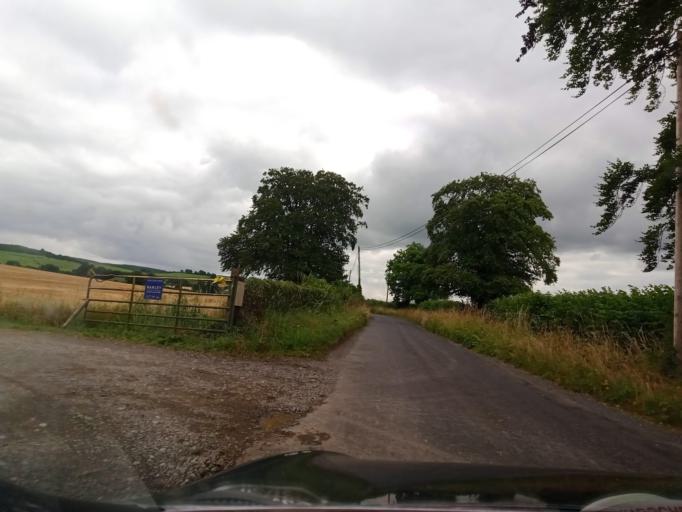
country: IE
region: Leinster
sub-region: Laois
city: Stradbally
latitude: 52.9868
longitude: -7.1746
